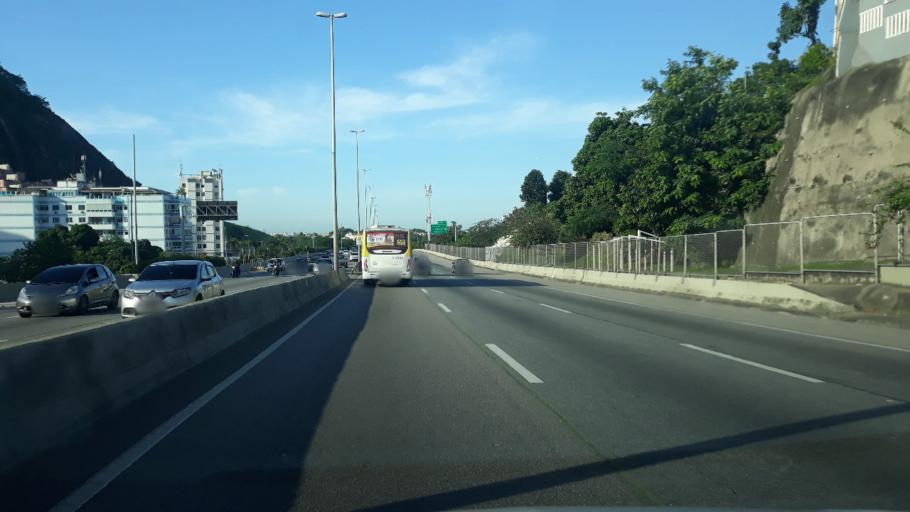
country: BR
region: Rio de Janeiro
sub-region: Sao Joao De Meriti
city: Sao Joao de Meriti
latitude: -22.9362
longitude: -43.3475
